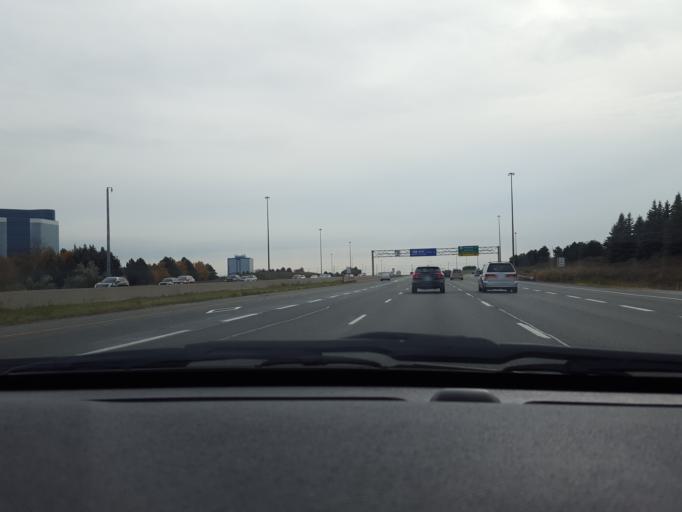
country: CA
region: Ontario
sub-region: York
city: Richmond Hill
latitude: 43.8543
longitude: -79.3730
